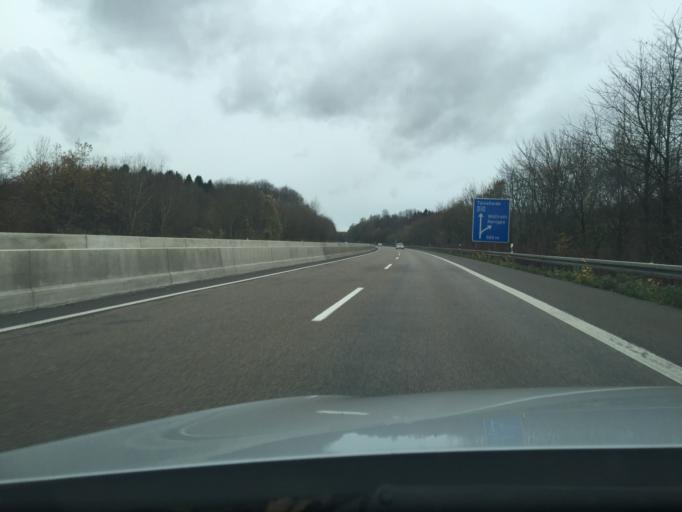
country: DE
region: North Rhine-Westphalia
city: Wulfrath
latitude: 51.2902
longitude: 7.0711
